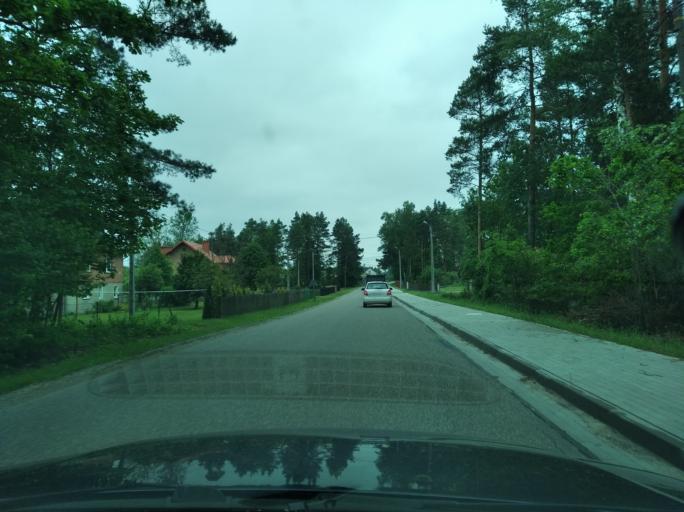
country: PL
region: Subcarpathian Voivodeship
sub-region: Powiat ropczycko-sedziszowski
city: Sedziszow Malopolski
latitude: 50.1439
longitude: 21.6700
